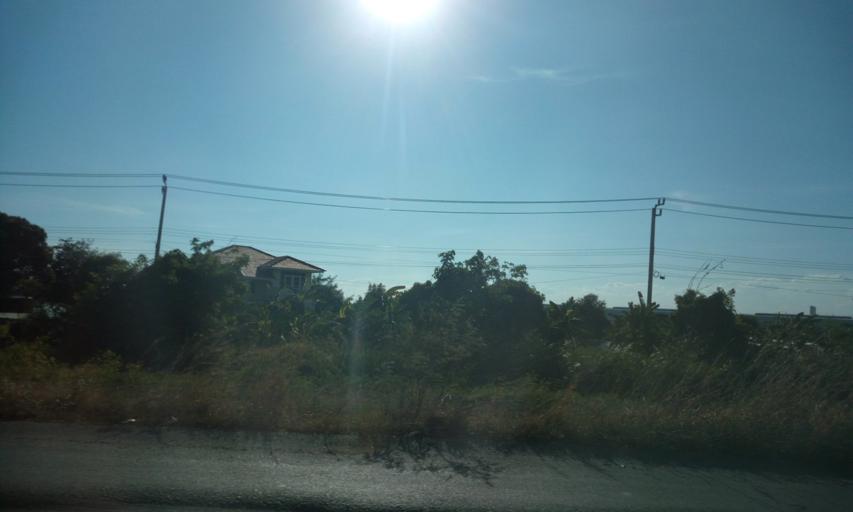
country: TH
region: Samut Prakan
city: Bang Bo District
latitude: 13.5710
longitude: 100.7564
